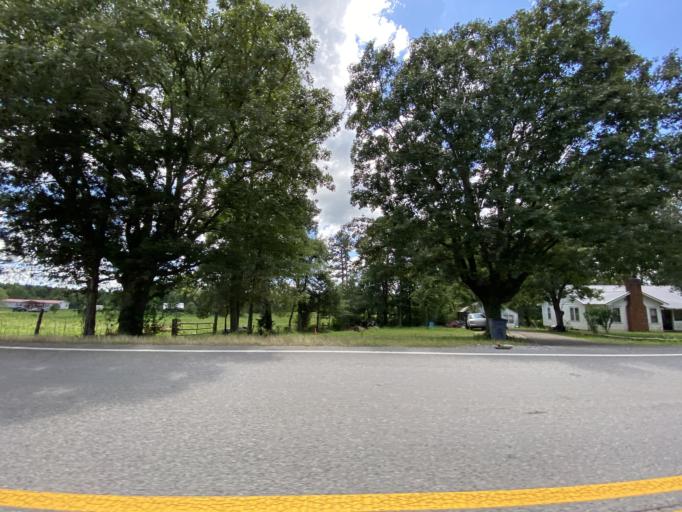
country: US
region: Alabama
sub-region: Lauderdale County
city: Underwood-Petersville
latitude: 34.9482
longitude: -87.8684
